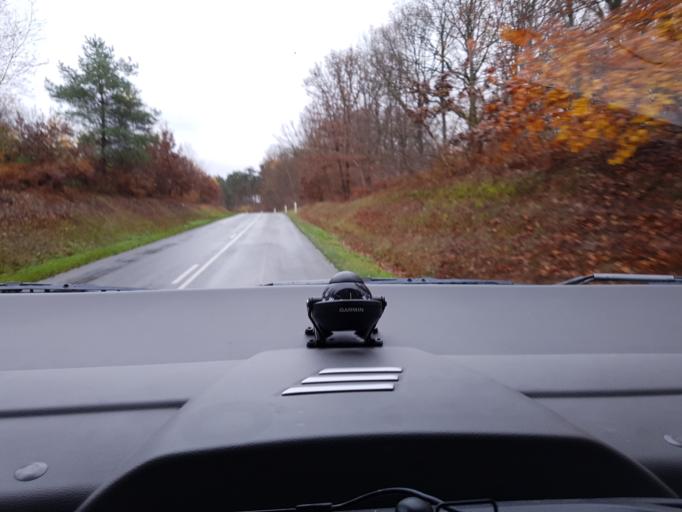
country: FR
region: Haute-Normandie
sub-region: Departement de l'Eure
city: Pont-Saint-Pierre
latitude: 49.3231
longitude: 1.2935
